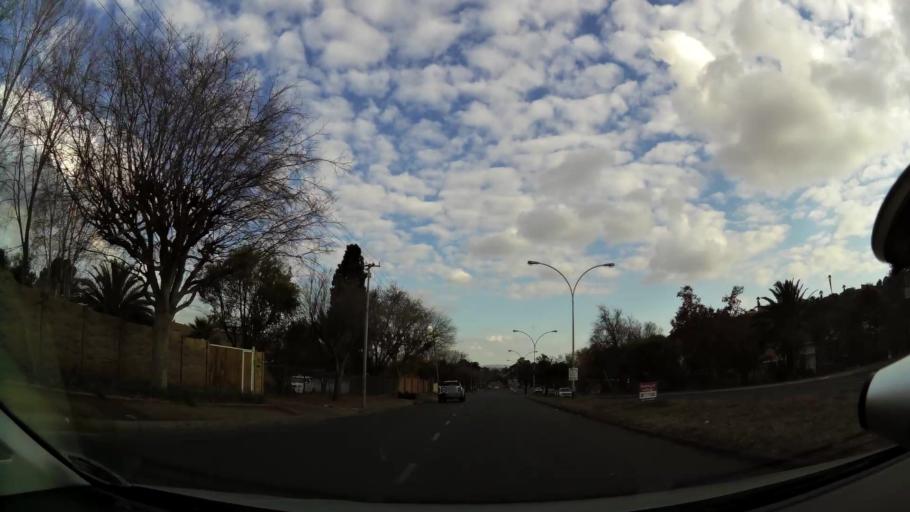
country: ZA
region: Orange Free State
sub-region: Mangaung Metropolitan Municipality
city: Bloemfontein
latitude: -29.0876
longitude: 26.2047
